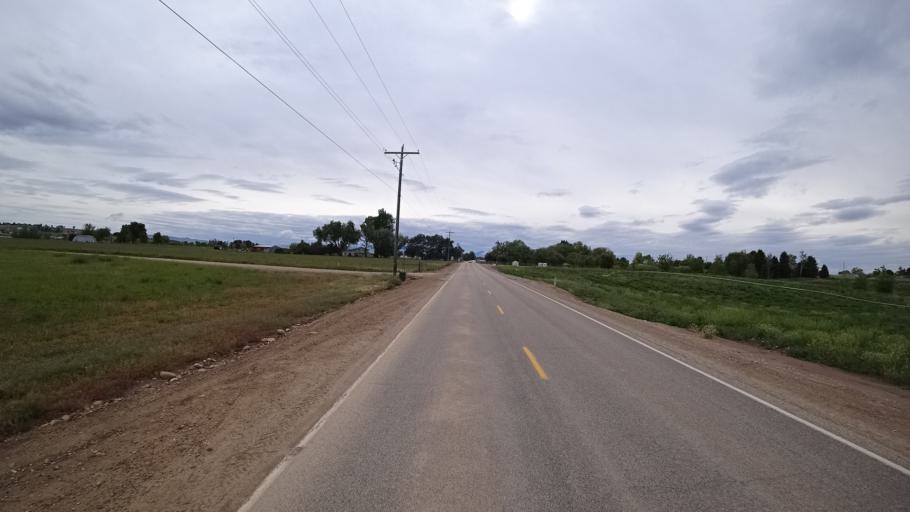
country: US
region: Idaho
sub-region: Ada County
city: Star
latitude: 43.7175
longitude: -116.4911
